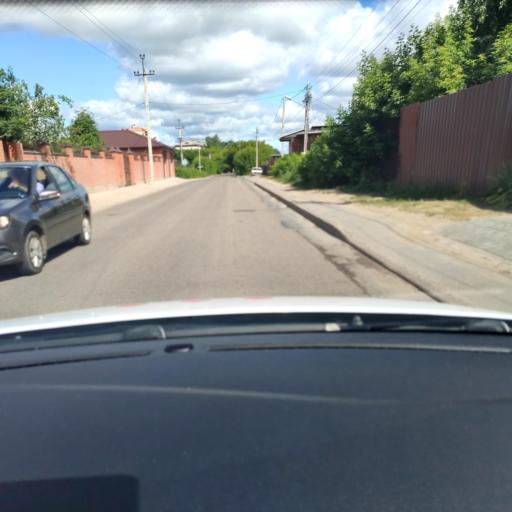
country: RU
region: Tatarstan
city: Vysokaya Gora
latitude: 55.8642
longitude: 49.2370
